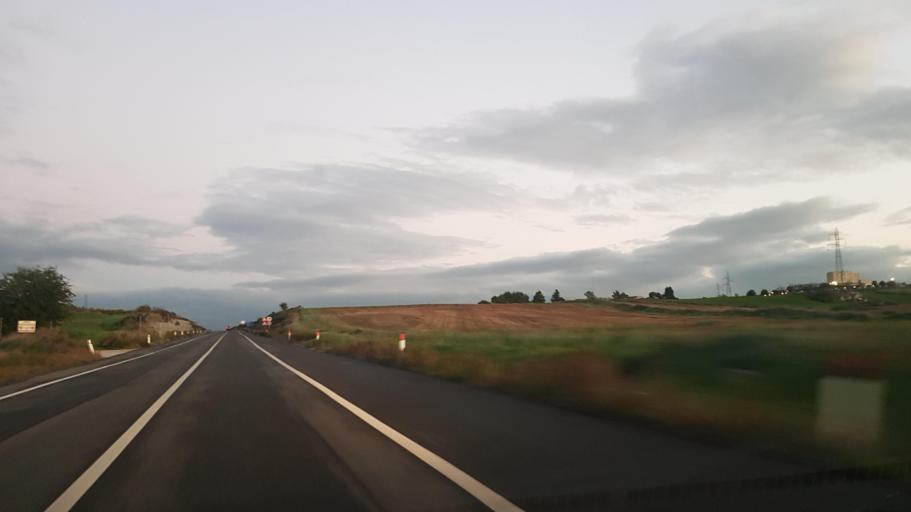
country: IT
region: Basilicate
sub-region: Provincia di Matera
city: Matera
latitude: 40.6727
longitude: 16.6854
